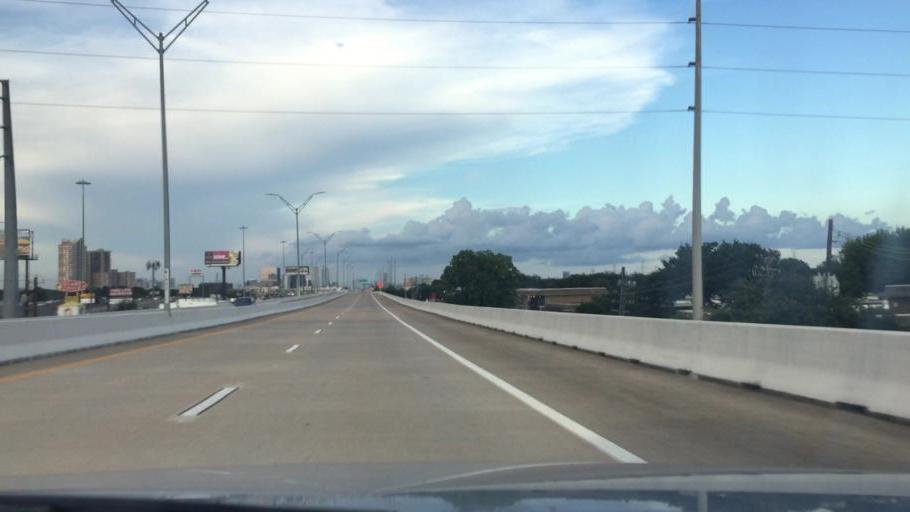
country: US
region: Texas
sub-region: Harris County
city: Bellaire
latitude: 29.7243
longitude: -95.4816
